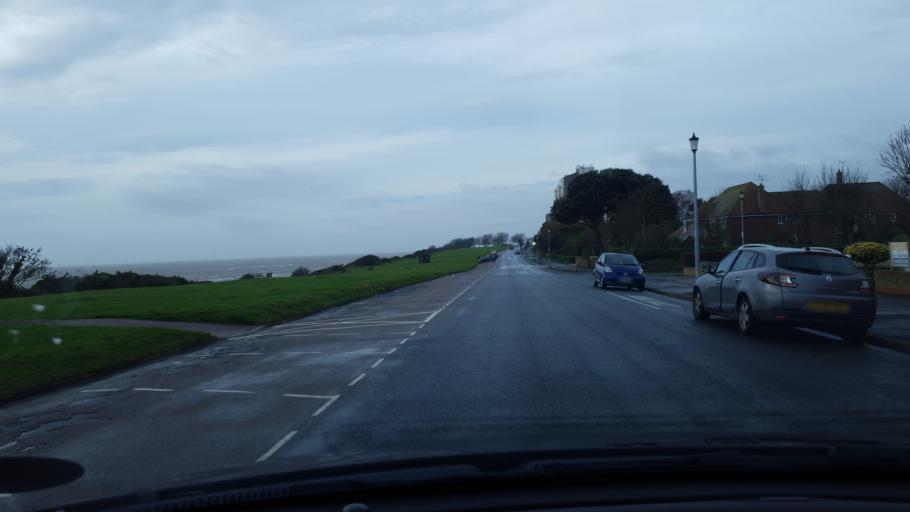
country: GB
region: England
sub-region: Essex
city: Frinton-on-Sea
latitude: 51.8336
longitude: 1.2525
